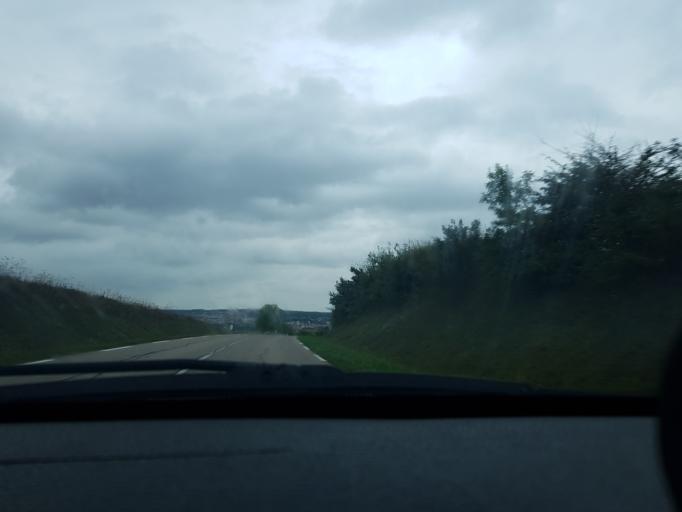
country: FR
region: Lorraine
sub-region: Departement de la Moselle
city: Faulquemont
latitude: 49.0218
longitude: 6.5933
